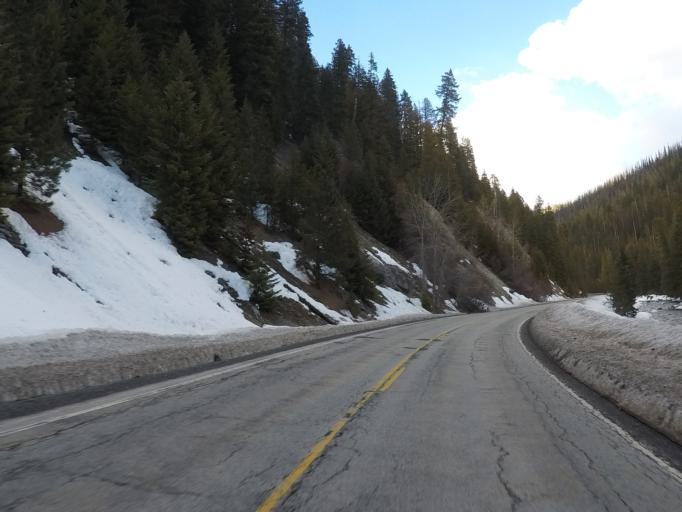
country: US
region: Montana
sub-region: Ravalli County
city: Stevensville
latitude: 46.5597
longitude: -114.6578
